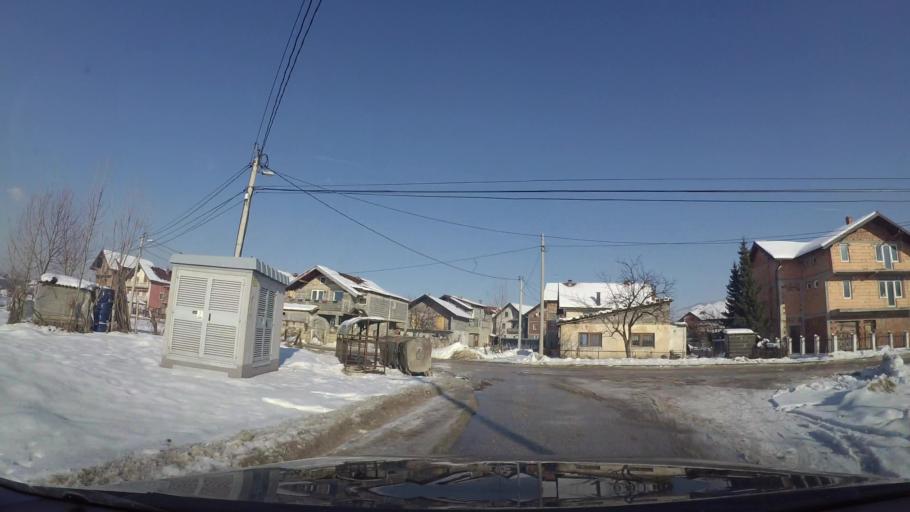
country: BA
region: Federation of Bosnia and Herzegovina
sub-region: Kanton Sarajevo
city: Sarajevo
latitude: 43.8094
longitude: 18.3279
